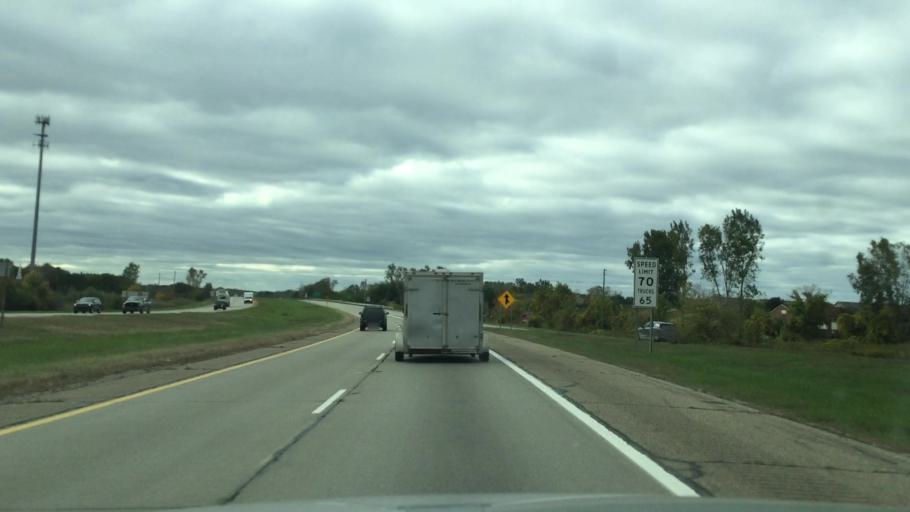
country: US
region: Michigan
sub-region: Macomb County
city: Shelby
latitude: 42.7328
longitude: -83.0267
